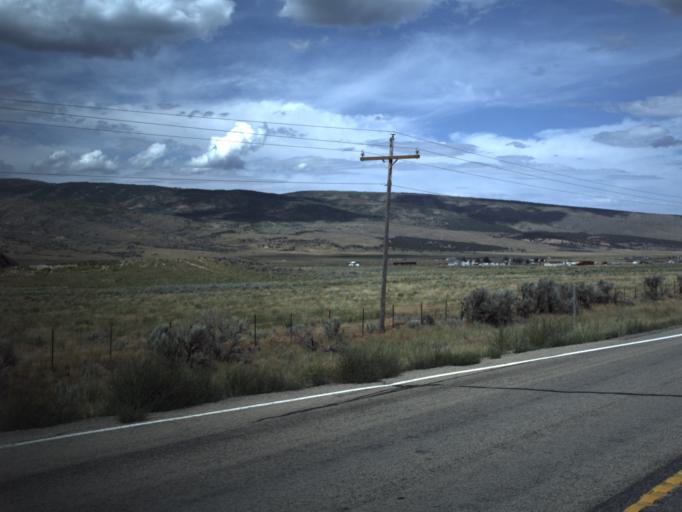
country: US
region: Utah
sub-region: Sanpete County
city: Fairview
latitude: 39.7602
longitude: -111.4825
